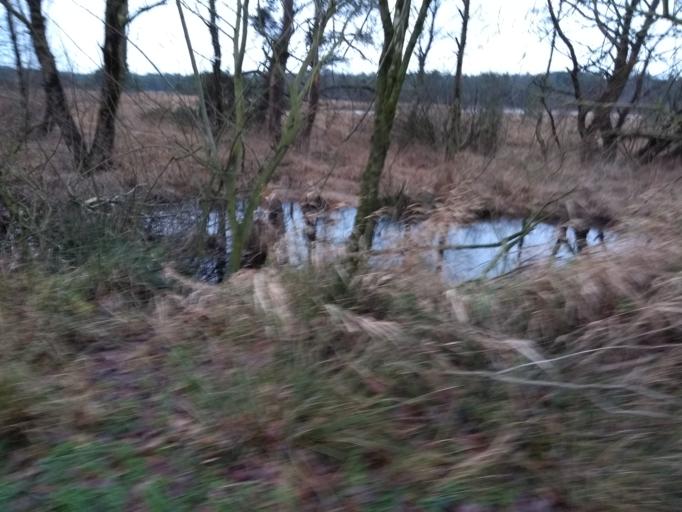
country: NL
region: Overijssel
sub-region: Gemeente Twenterand
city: Magele
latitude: 52.5045
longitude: 6.5481
